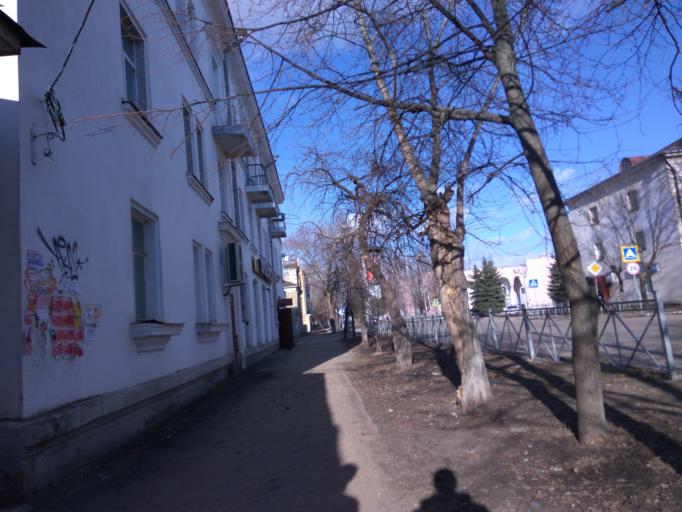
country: RU
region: Jaroslavl
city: Rostov
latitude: 57.1896
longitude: 39.4318
